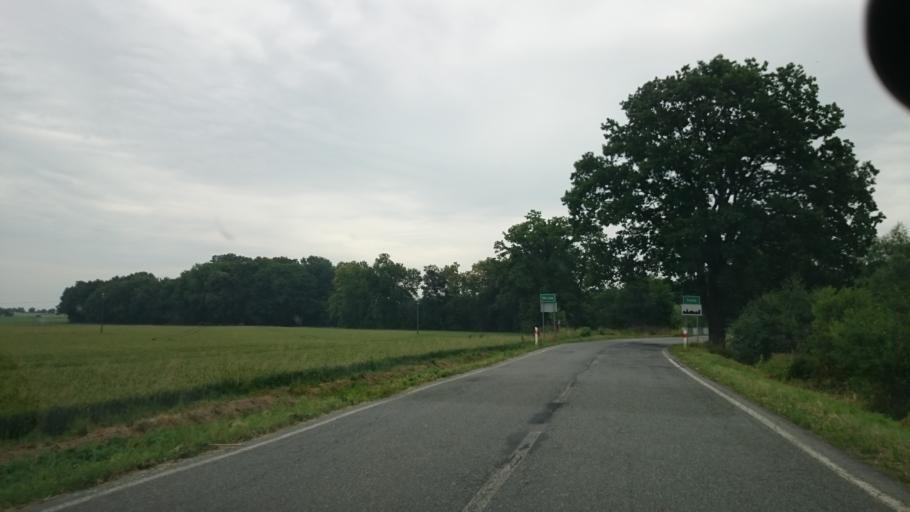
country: PL
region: Lower Silesian Voivodeship
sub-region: Powiat strzelinski
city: Przeworno
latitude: 50.6469
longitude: 17.1685
